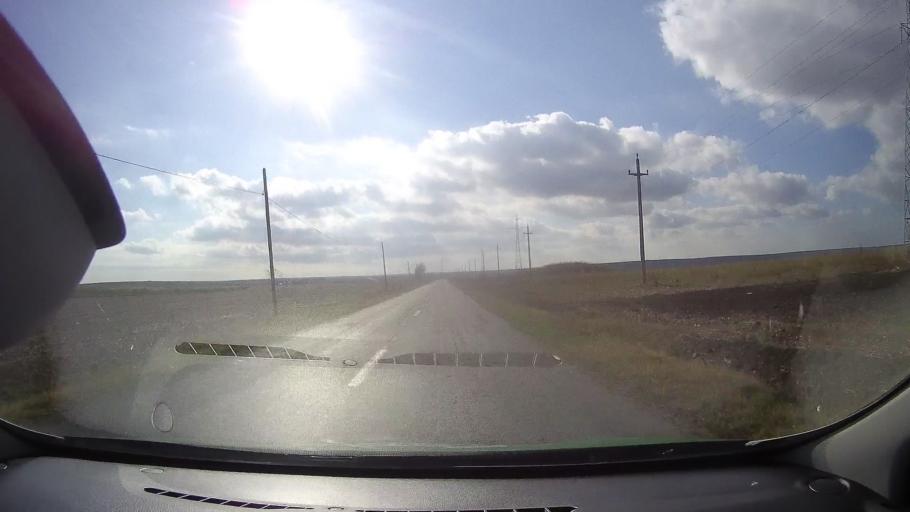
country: RO
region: Constanta
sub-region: Comuna Istria
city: Nuntasi
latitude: 44.5376
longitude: 28.6877
